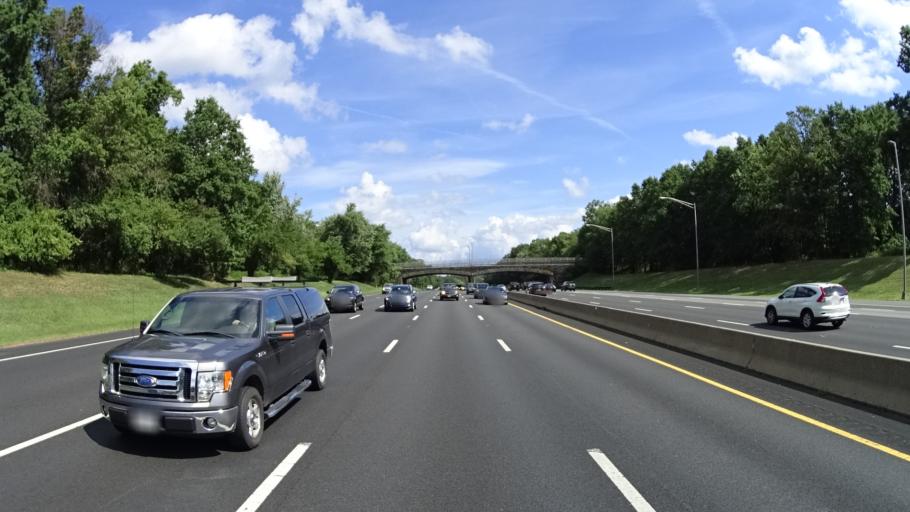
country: US
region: New Jersey
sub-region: Union County
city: Clark
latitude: 40.6139
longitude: -74.3119
